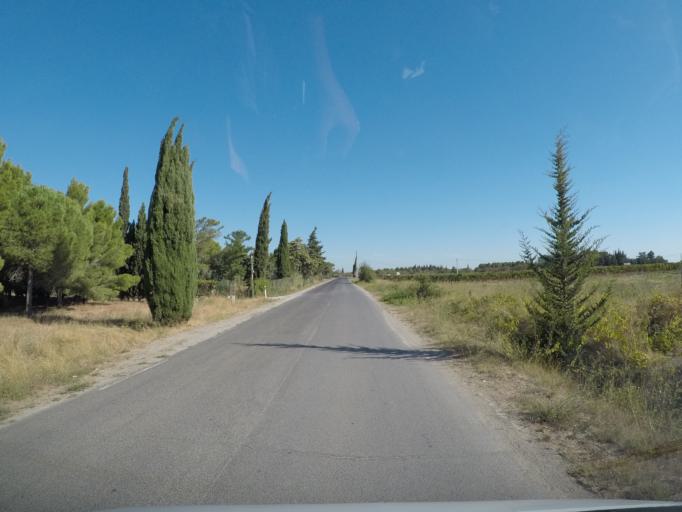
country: FR
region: Languedoc-Roussillon
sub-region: Departement de l'Aude
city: Narbonne
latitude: 43.1454
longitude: 3.0037
